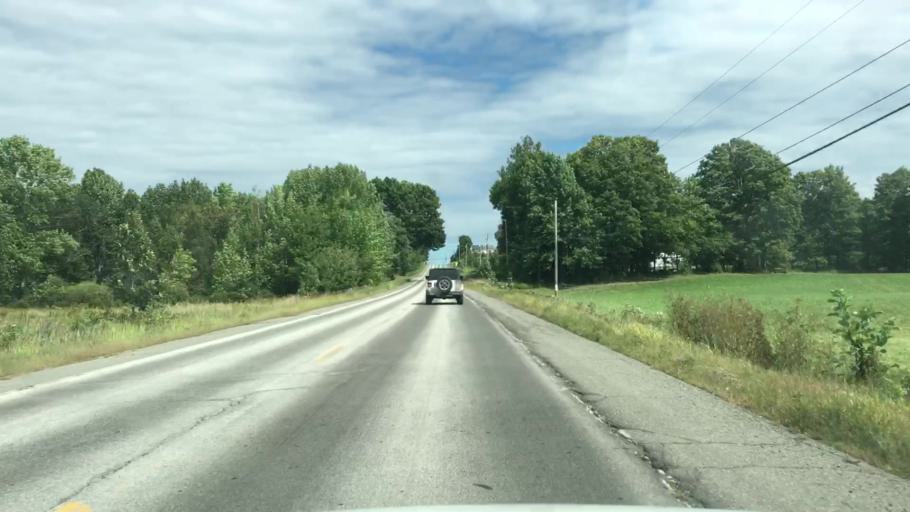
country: US
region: Maine
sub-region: Piscataquis County
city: Dover-Foxcroft
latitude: 45.1588
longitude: -69.2331
